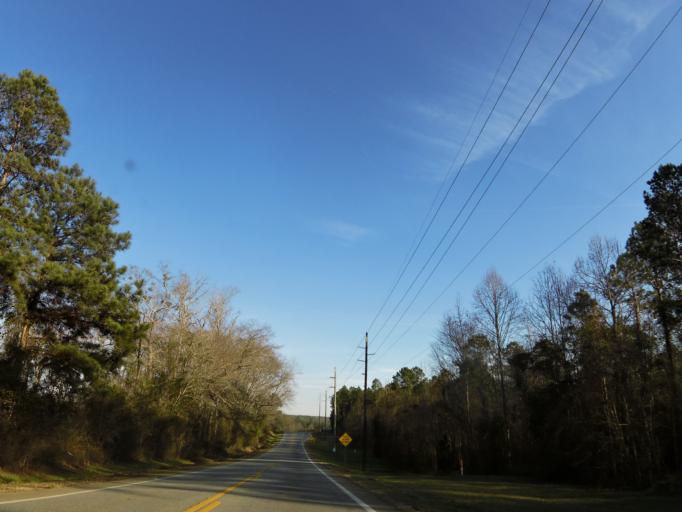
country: US
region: Georgia
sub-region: Webster County
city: Preston
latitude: 32.0456
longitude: -84.4930
